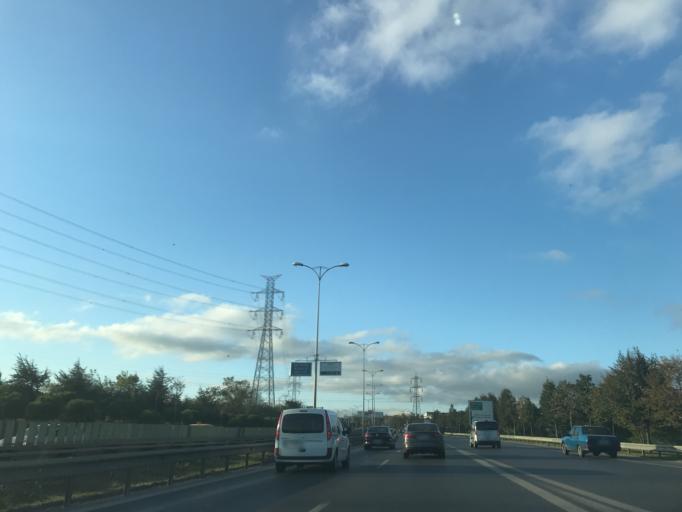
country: TR
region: Istanbul
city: Esenler
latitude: 41.0607
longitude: 28.8854
